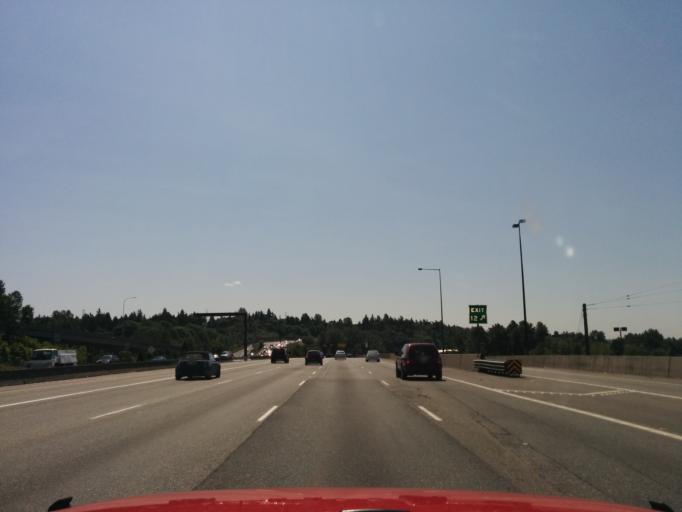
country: US
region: Washington
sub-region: King County
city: Bellevue
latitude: 47.6050
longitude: -122.1858
